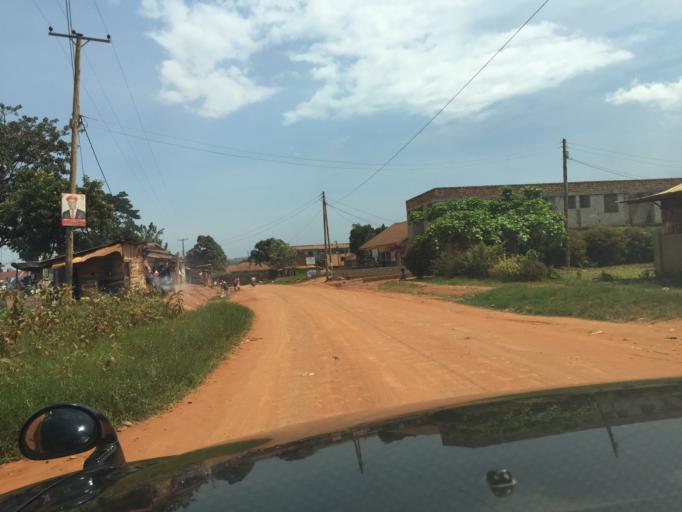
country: UG
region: Central Region
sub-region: Wakiso District
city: Kireka
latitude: 0.4016
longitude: 32.6207
